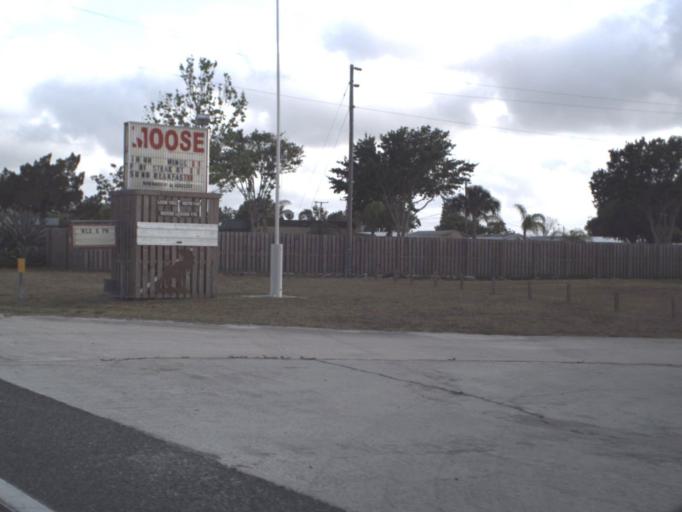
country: US
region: Florida
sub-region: Brevard County
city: Mims
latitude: 28.6911
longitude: -80.8572
